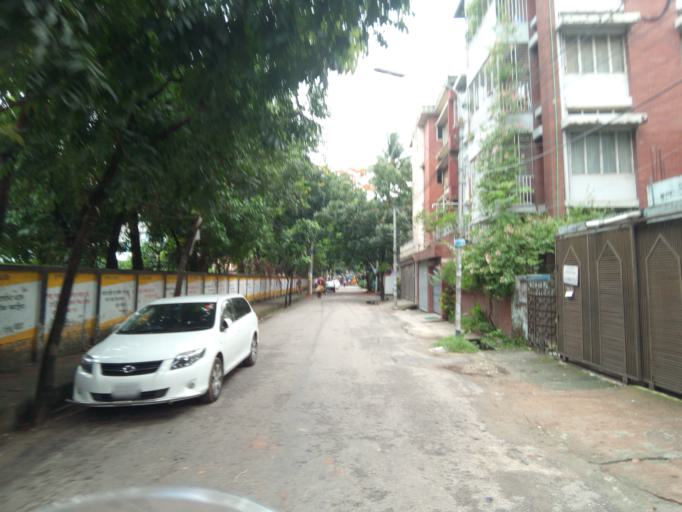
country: BD
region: Dhaka
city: Azimpur
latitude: 23.7567
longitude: 90.3719
